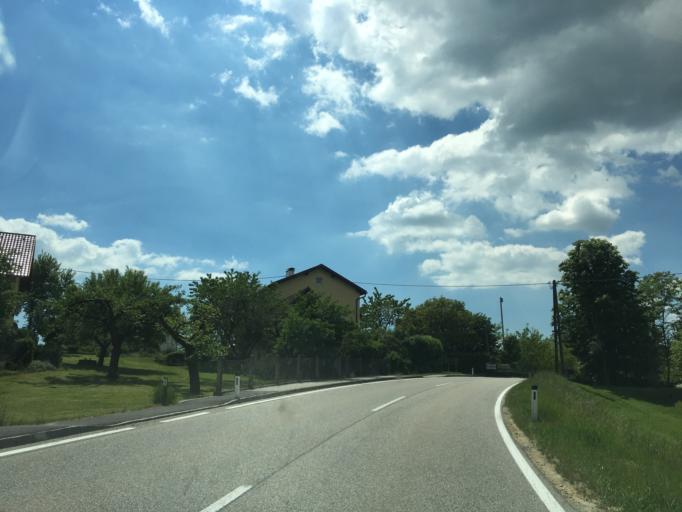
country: AT
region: Upper Austria
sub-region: Politischer Bezirk Urfahr-Umgebung
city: Engerwitzdorf
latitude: 48.3698
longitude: 14.5421
